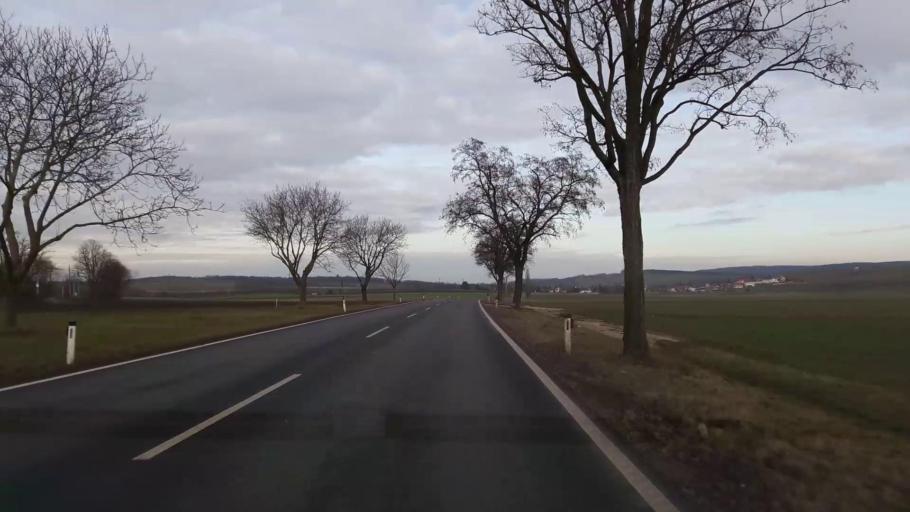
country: AT
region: Lower Austria
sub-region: Politischer Bezirk Mistelbach
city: Mistelbach
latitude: 48.5924
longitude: 16.5486
